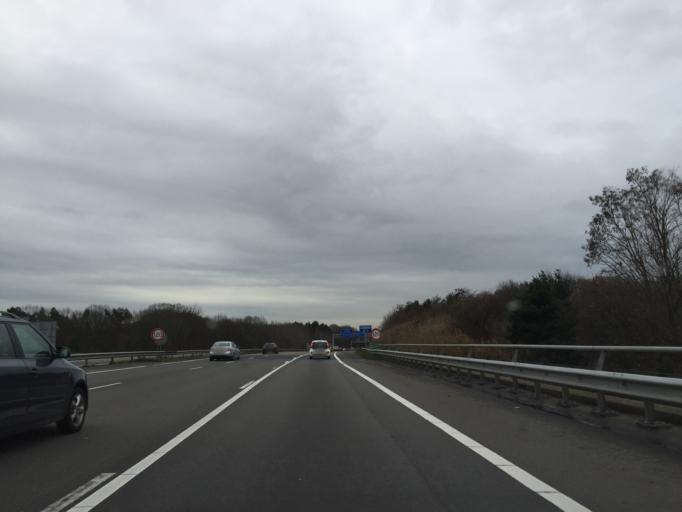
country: NL
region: North Brabant
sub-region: Gemeente Bergen op Zoom
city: Bergen op Zoom
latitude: 51.4989
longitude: 4.3152
